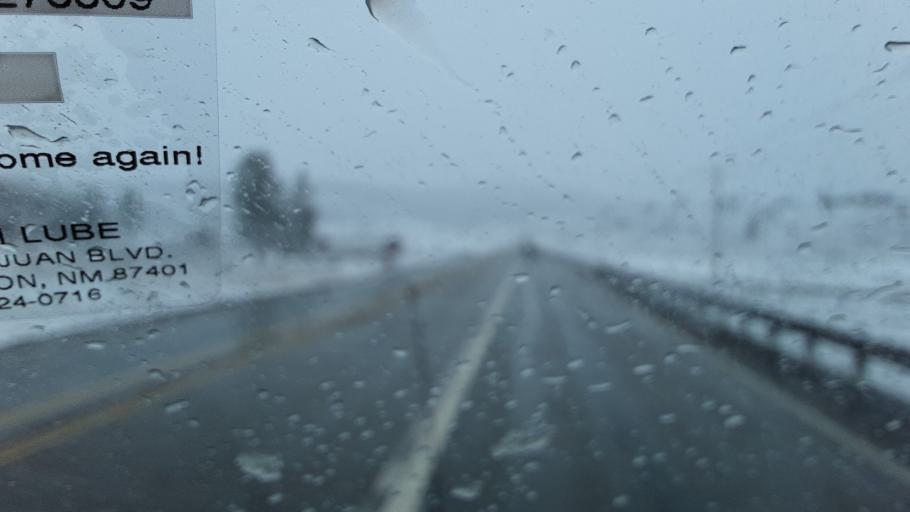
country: US
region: Colorado
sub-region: Archuleta County
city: Pagosa Springs
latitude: 37.2434
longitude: -106.9891
